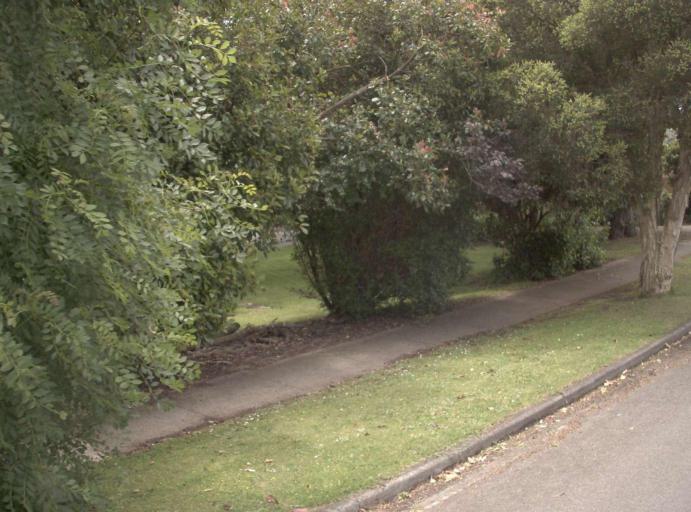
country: AU
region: Victoria
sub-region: Baw Baw
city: Warragul
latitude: -38.1457
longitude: 145.9376
